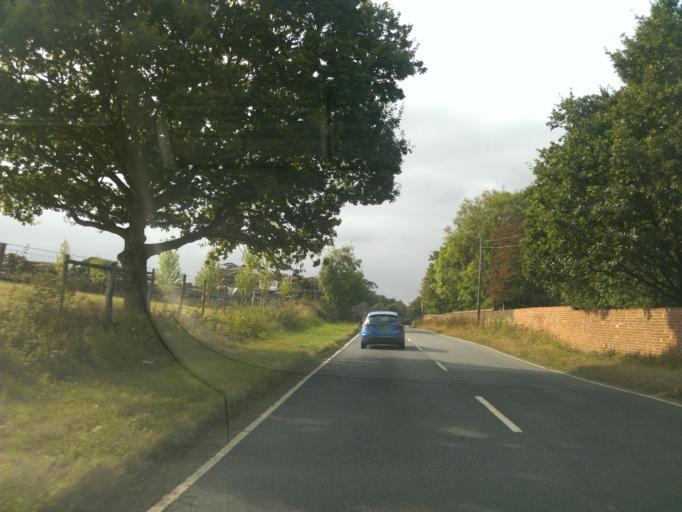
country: GB
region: England
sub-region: Essex
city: Great Totham
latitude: 51.8014
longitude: 0.6912
